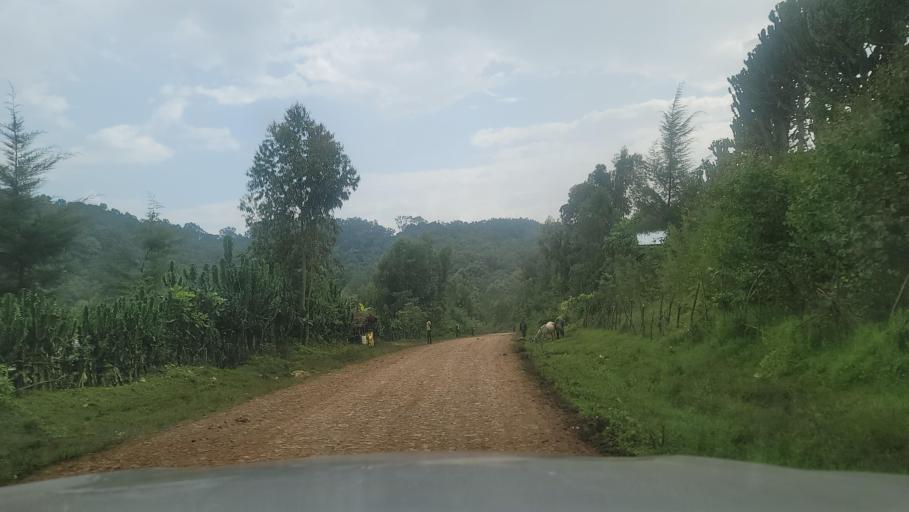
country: ET
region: Southern Nations, Nationalities, and People's Region
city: Bonga
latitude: 7.6913
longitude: 36.2442
